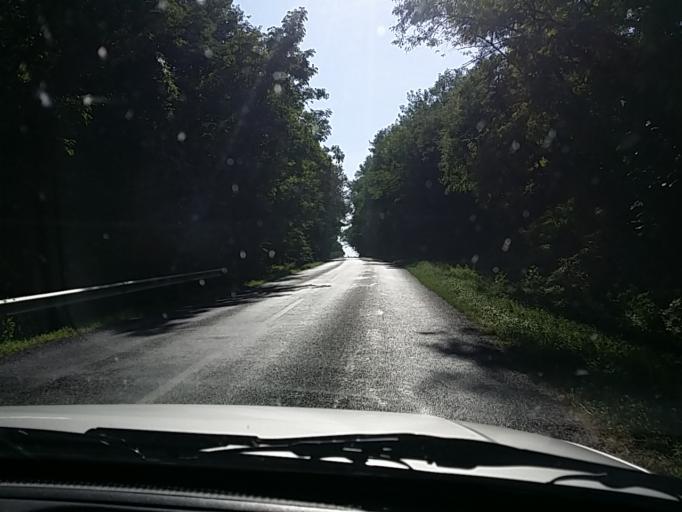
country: AT
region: Burgenland
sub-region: Politischer Bezirk Oberpullendorf
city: Lutzmannsburg
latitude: 47.4396
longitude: 16.6709
